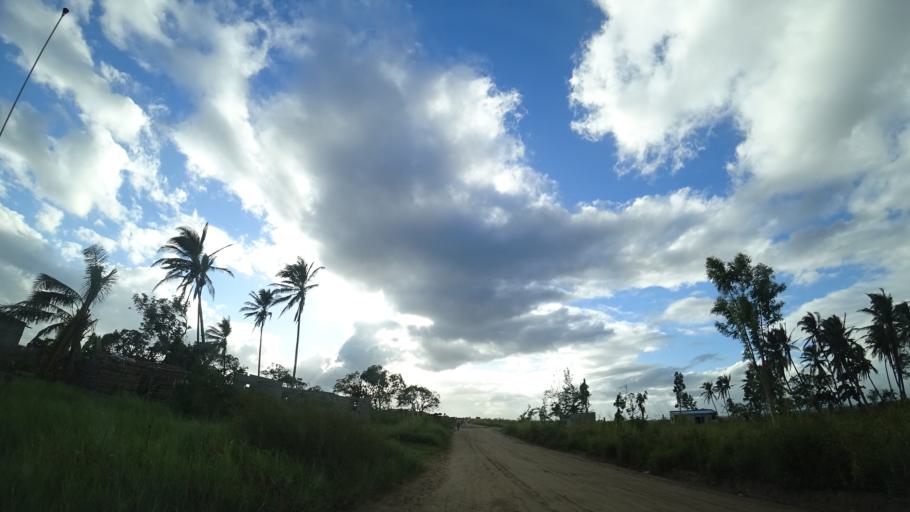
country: MZ
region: Sofala
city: Beira
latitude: -19.7640
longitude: 34.8999
